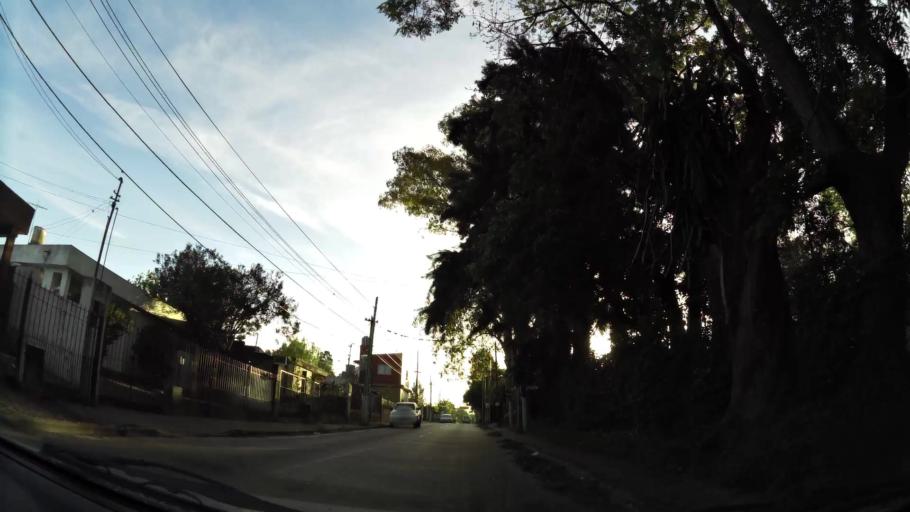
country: AR
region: Buenos Aires
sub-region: Partido de Quilmes
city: Quilmes
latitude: -34.7783
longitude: -58.1959
